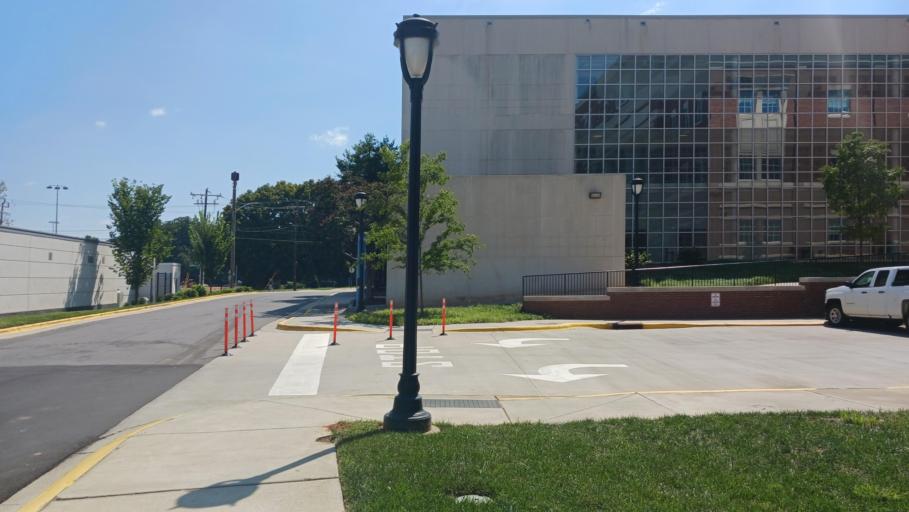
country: US
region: North Carolina
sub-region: Mecklenburg County
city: Charlotte
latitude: 35.2175
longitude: -80.8281
